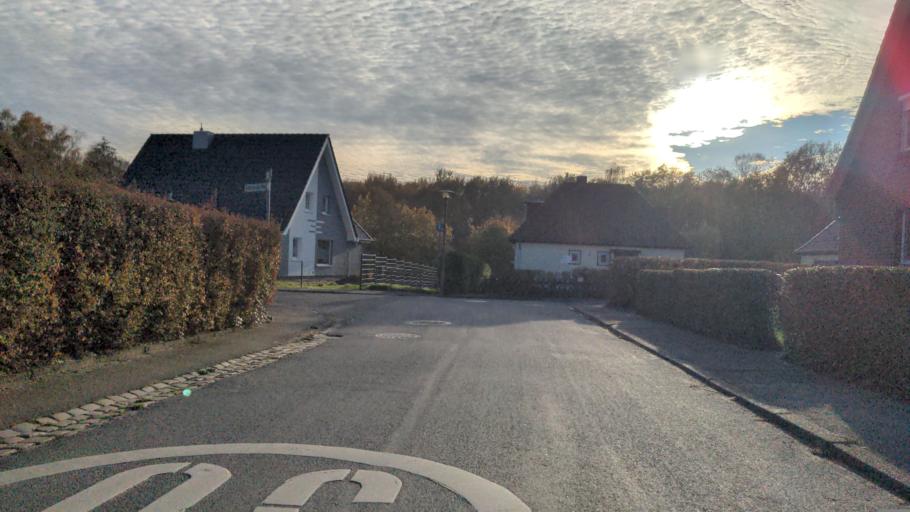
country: DE
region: Schleswig-Holstein
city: Gross Gronau
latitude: 53.8430
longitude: 10.7420
